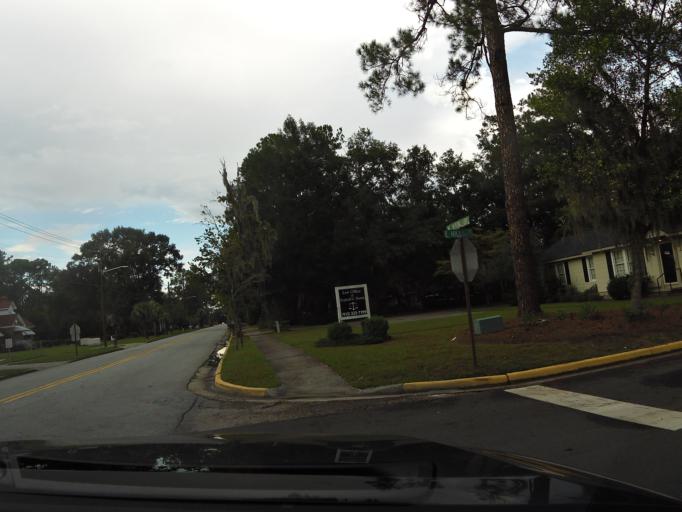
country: US
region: Georgia
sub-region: Liberty County
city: Hinesville
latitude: 31.8525
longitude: -81.5950
